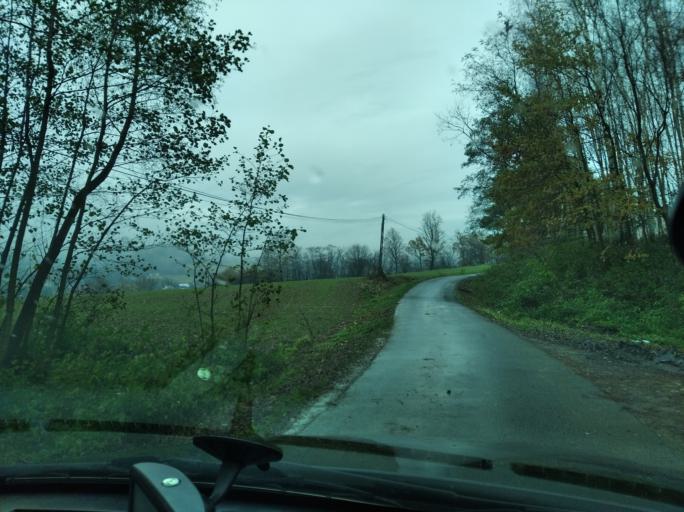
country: PL
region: Subcarpathian Voivodeship
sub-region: Powiat strzyzowski
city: Babica
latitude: 49.9307
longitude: 21.8815
